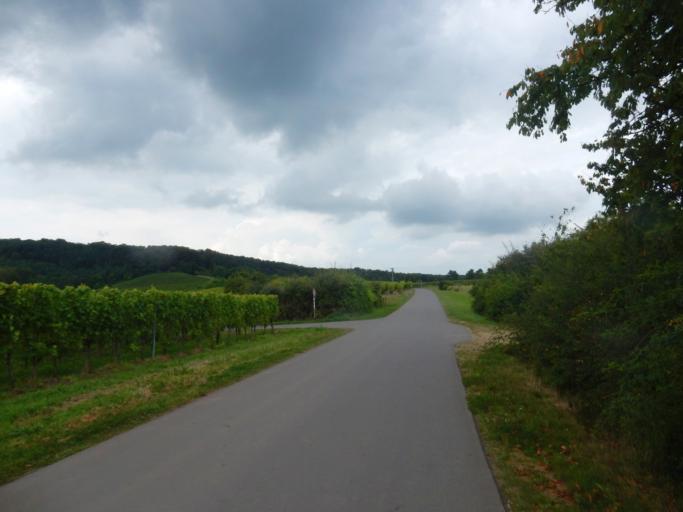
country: LU
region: Grevenmacher
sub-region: Canton de Remich
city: Stadtbredimus
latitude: 49.5716
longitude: 6.3505
